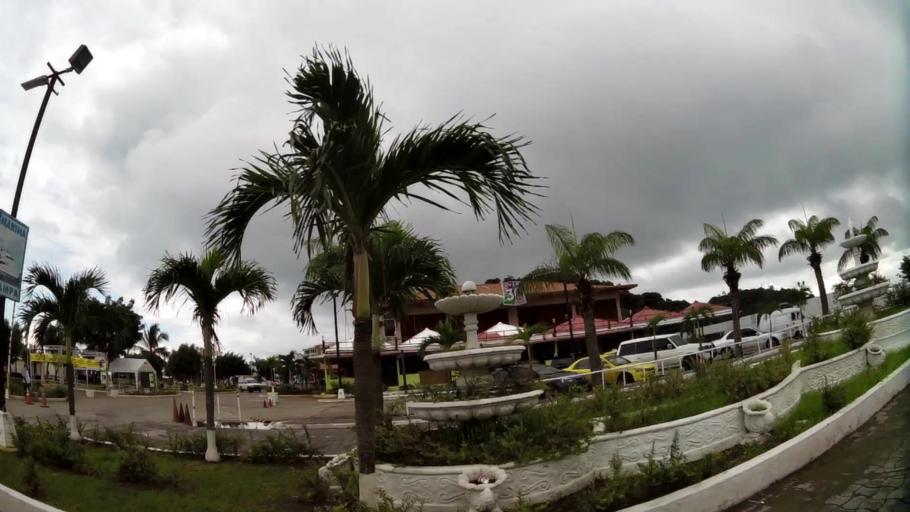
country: PA
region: Panama
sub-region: Distrito de Panama
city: Ancon
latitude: 8.9154
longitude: -79.5280
